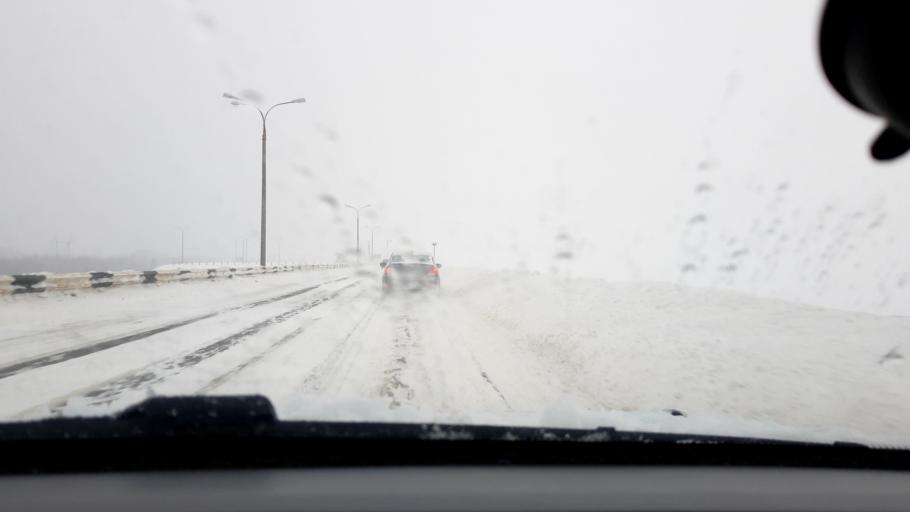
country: RU
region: Nizjnij Novgorod
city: Pervomayskiy
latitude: 56.6442
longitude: 43.3319
